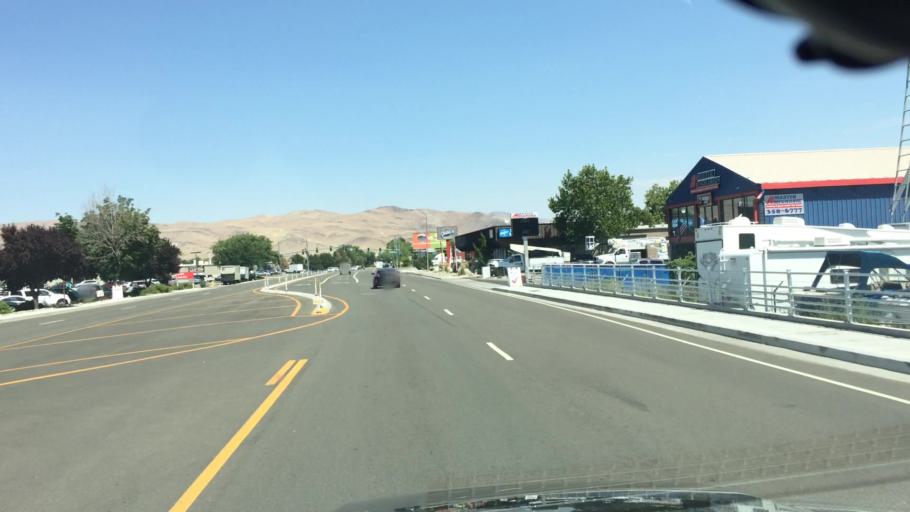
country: US
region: Nevada
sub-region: Washoe County
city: Sparks
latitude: 39.5274
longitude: -119.7426
